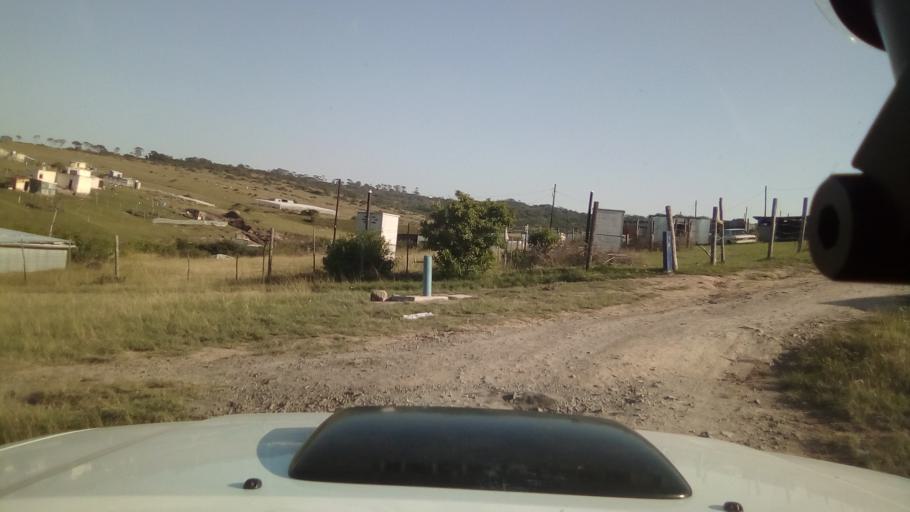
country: ZA
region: Eastern Cape
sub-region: Buffalo City Metropolitan Municipality
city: East London
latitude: -32.8485
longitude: 27.9874
